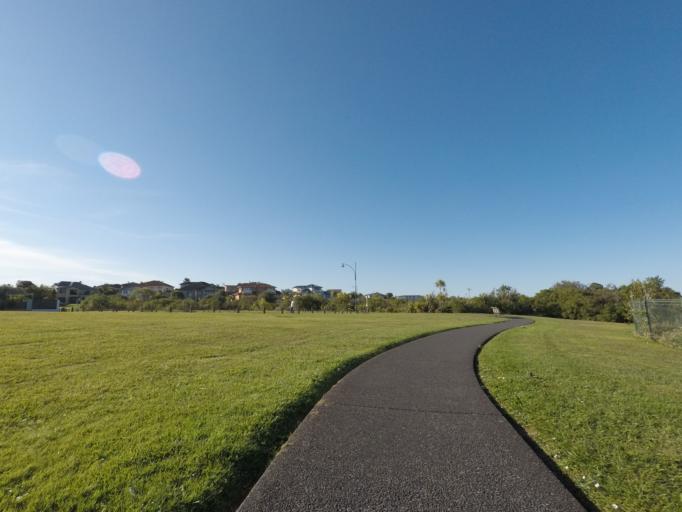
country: NZ
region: Auckland
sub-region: Auckland
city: Rosebank
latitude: -36.8386
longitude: 174.6613
